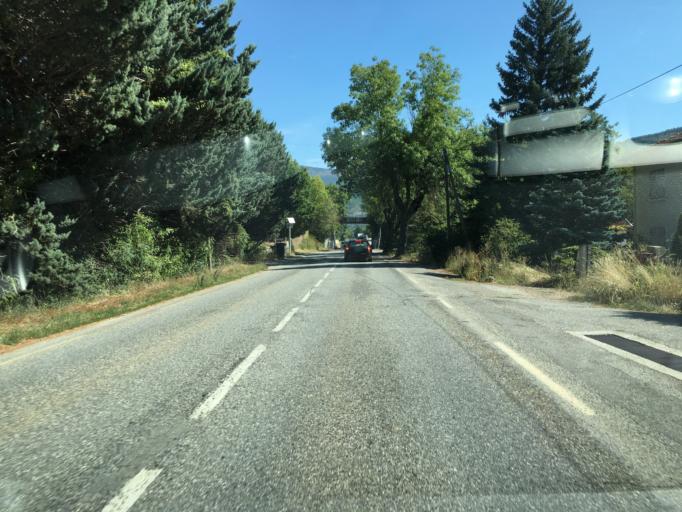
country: FR
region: Provence-Alpes-Cote d'Azur
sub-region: Departement des Hautes-Alpes
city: Veynes
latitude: 44.5266
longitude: 5.7629
